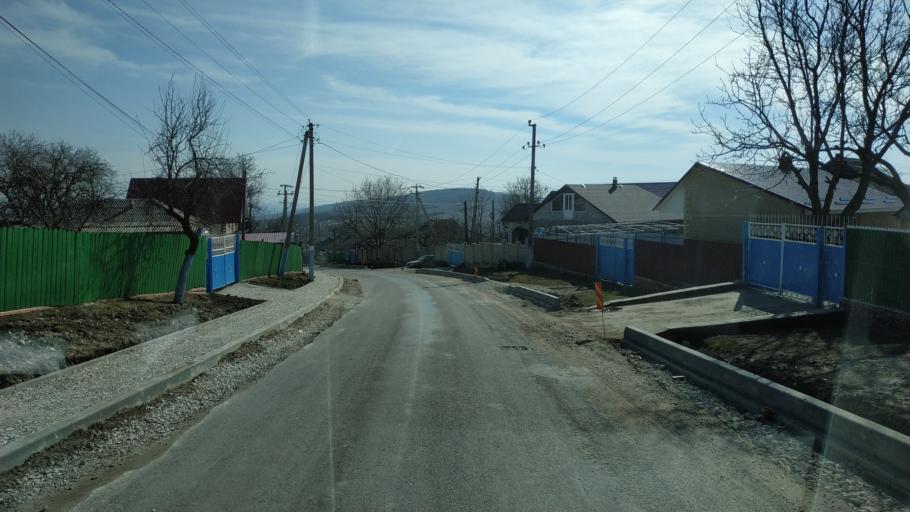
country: MD
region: Nisporeni
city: Nisporeni
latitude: 47.2002
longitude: 28.0615
